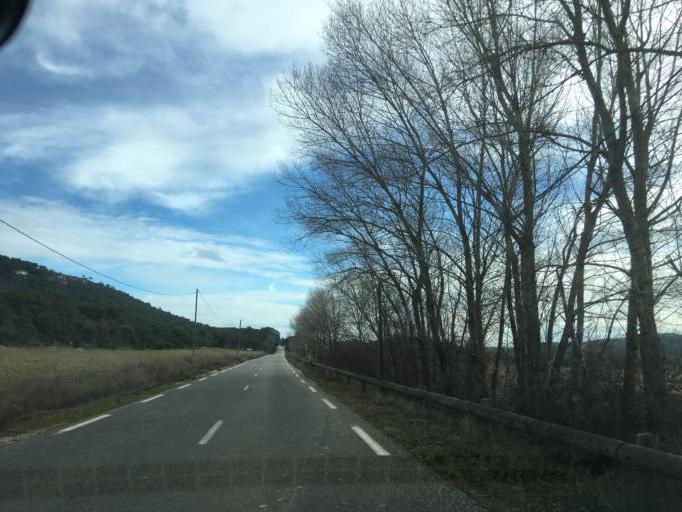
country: FR
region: Provence-Alpes-Cote d'Azur
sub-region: Departement du Var
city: Bras
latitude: 43.4460
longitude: 6.0069
